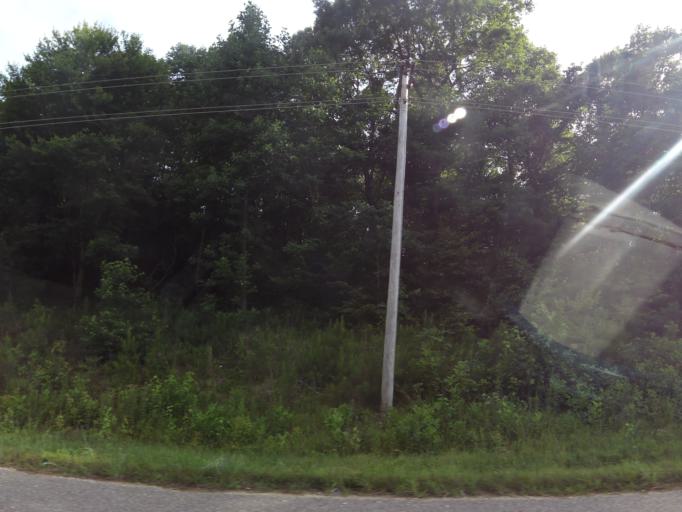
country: US
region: Tennessee
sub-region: Benton County
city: Camden
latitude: 36.0424
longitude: -88.1378
